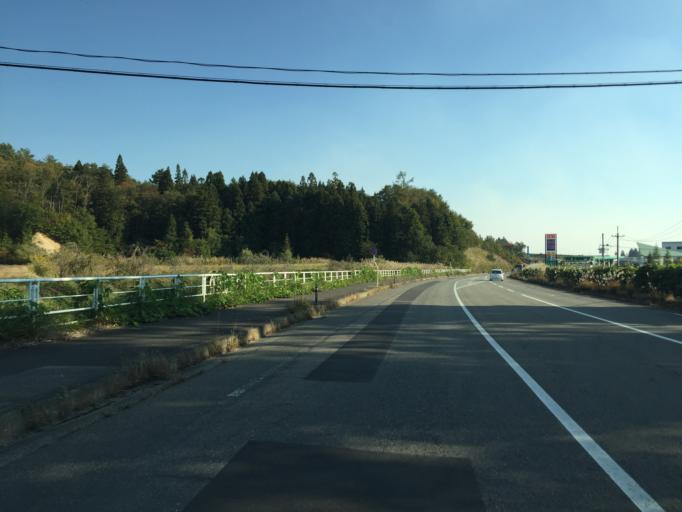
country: JP
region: Fukushima
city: Kitakata
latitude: 37.6932
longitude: 139.8896
